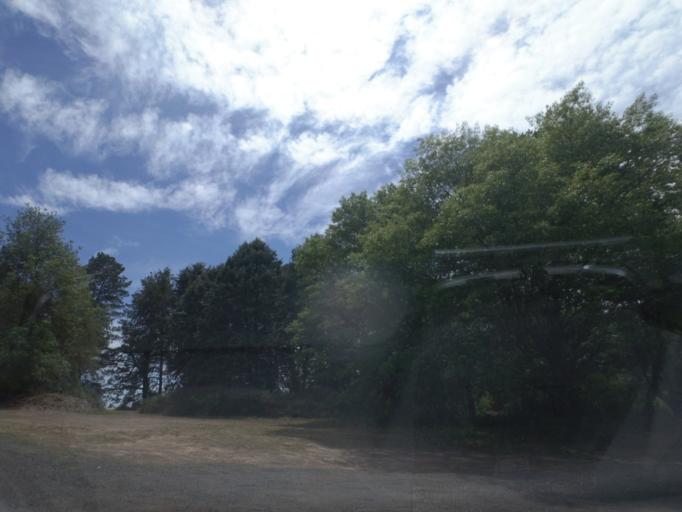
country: AU
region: New South Wales
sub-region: Yass Valley
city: Gundaroo
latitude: -34.9990
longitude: 149.3824
